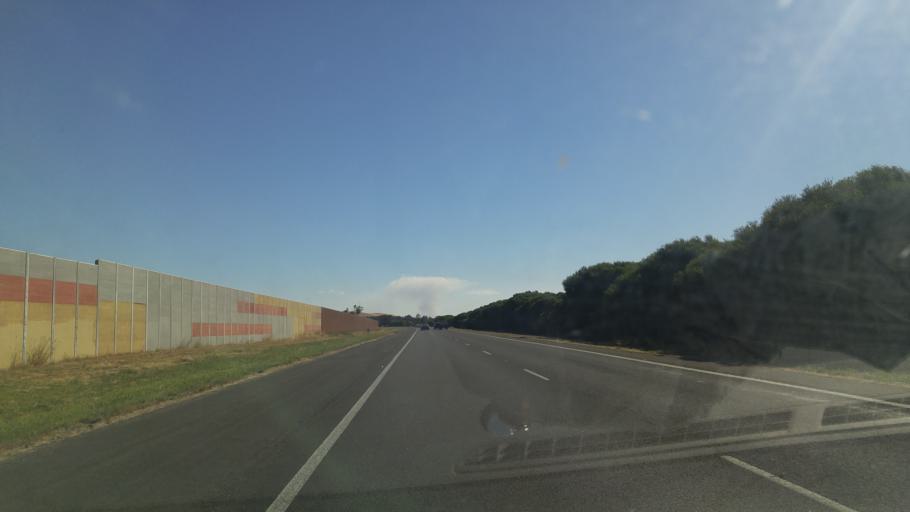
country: AU
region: Victoria
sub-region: Whittlesea
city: Whittlesea
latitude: -37.4248
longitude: 144.9885
